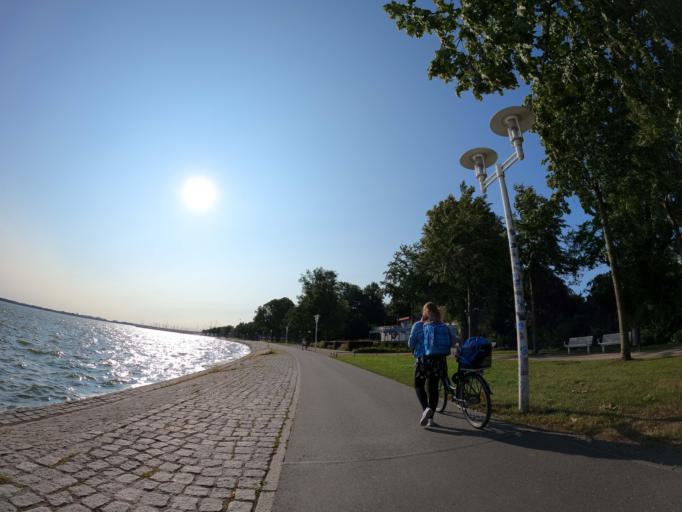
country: DE
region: Mecklenburg-Vorpommern
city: Stralsund
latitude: 54.3200
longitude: 13.0880
